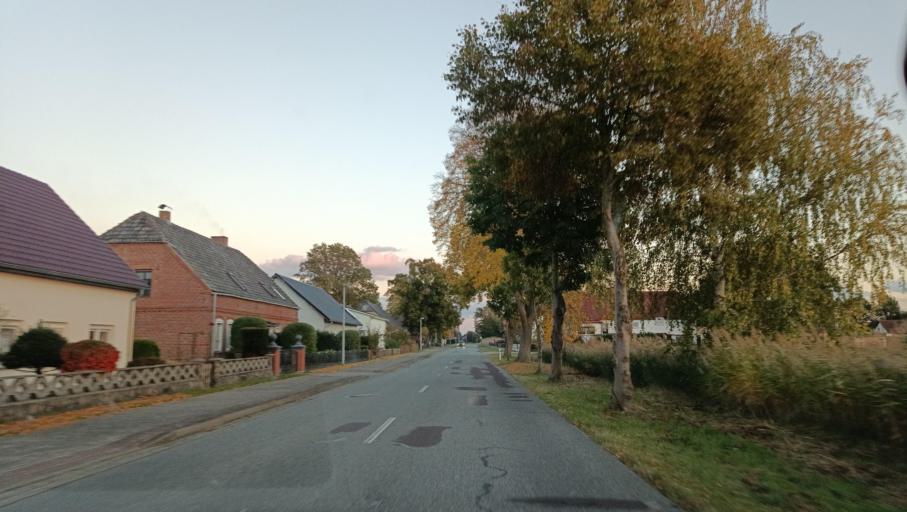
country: DE
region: Mecklenburg-Vorpommern
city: Ludwigslust
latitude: 53.2835
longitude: 11.4832
